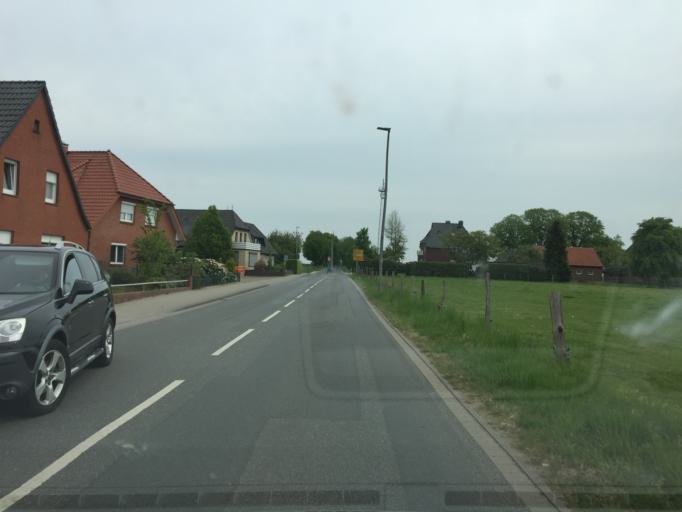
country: DE
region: Lower Saxony
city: Syke
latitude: 52.9071
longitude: 8.7966
